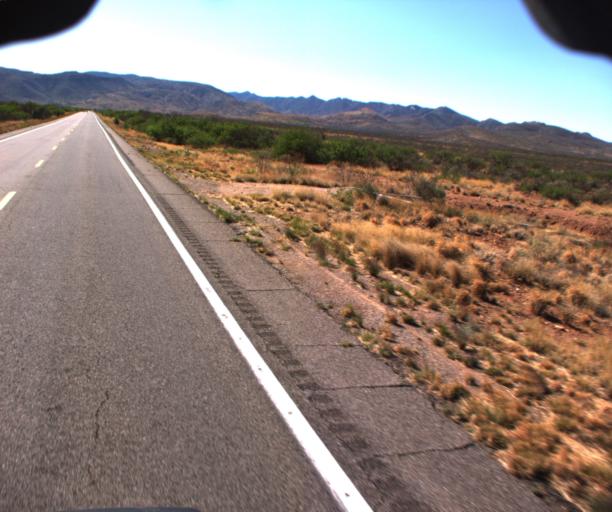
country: US
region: Arizona
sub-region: Cochise County
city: Bisbee
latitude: 31.5595
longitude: -110.0203
